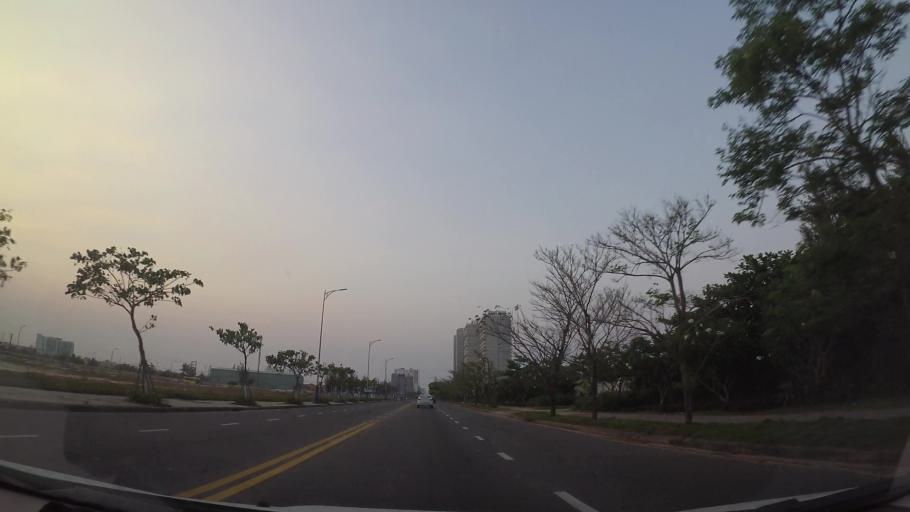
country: VN
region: Da Nang
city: Ngu Hanh Son
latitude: 16.0202
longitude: 108.2587
